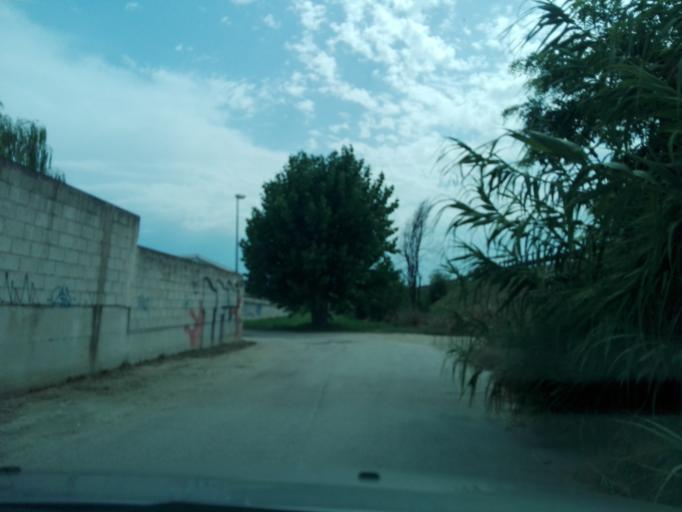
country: IT
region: Abruzzo
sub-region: Provincia di Pescara
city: Cappelle sul Tavo
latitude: 42.4868
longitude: 14.1112
